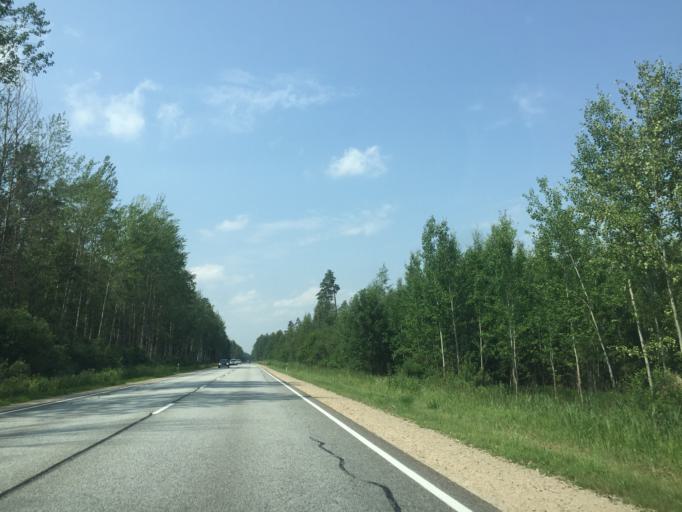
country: LV
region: Kekava
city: Balozi
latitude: 56.8179
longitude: 24.1145
